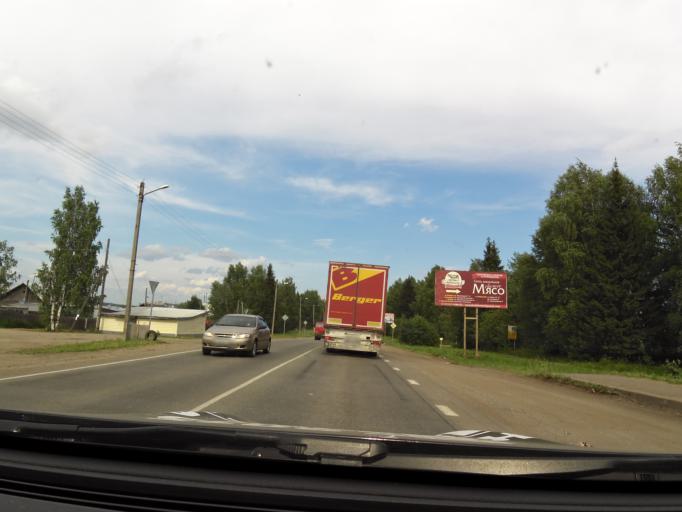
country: RU
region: Kirov
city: Stulovo
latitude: 58.7158
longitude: 50.1275
